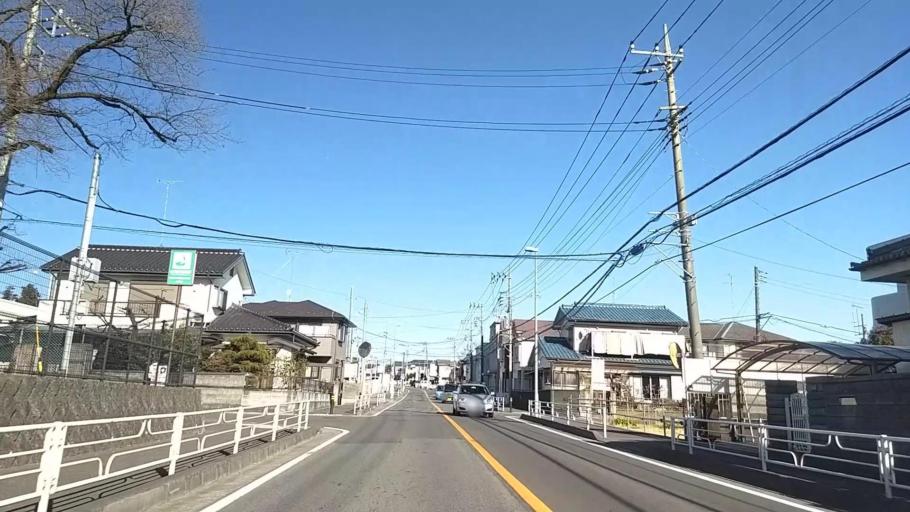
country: JP
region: Tokyo
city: Hachioji
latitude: 35.5974
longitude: 139.3027
